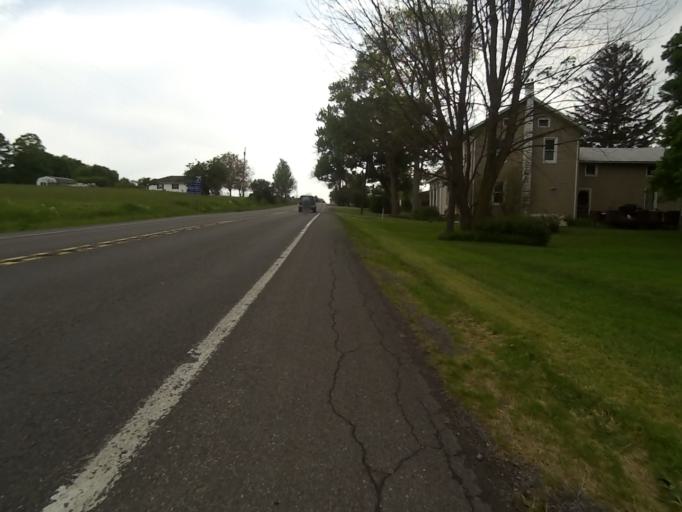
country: US
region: Pennsylvania
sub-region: Centre County
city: Zion
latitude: 40.9435
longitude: -77.6381
